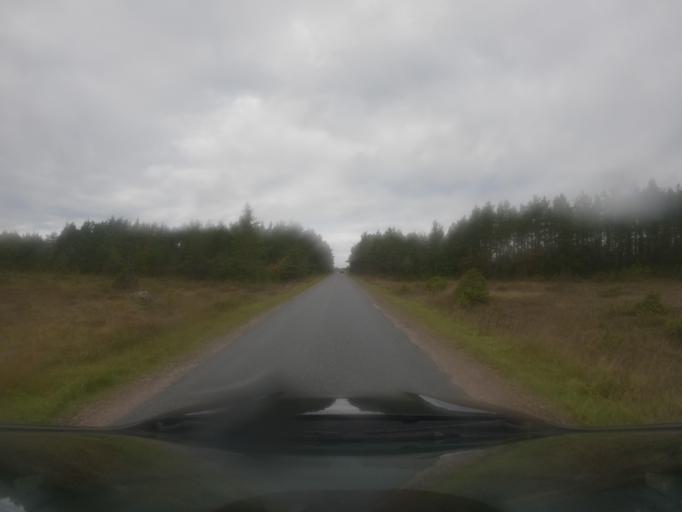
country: EE
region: Saare
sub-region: Kuressaare linn
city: Kuressaare
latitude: 58.4414
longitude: 21.9876
